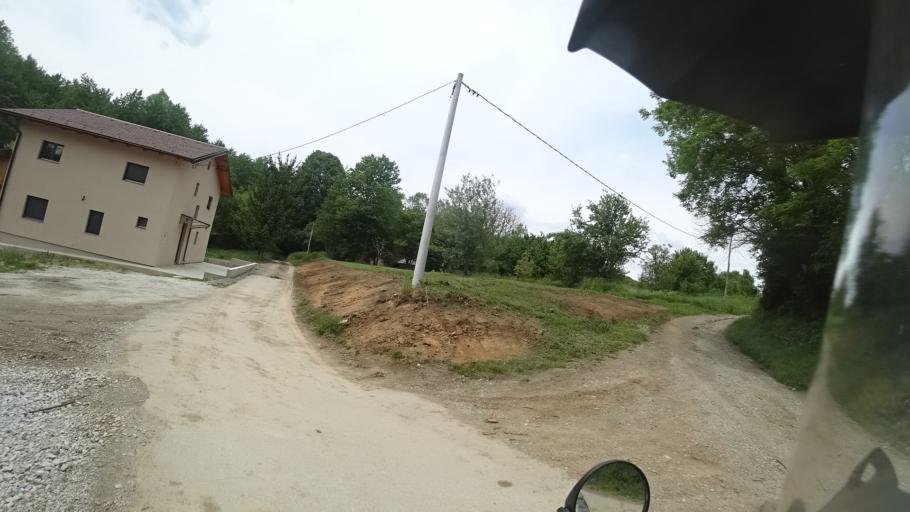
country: HR
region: Karlovacka
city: Vojnic
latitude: 45.2477
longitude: 15.6634
